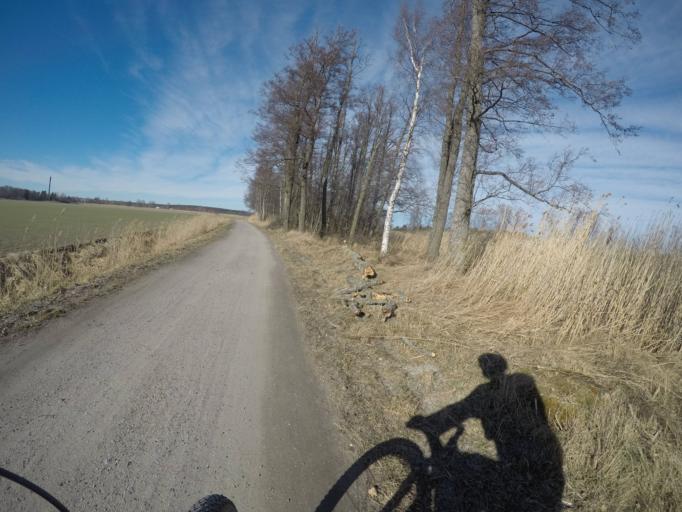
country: SE
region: Soedermanland
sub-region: Eskilstuna Kommun
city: Torshalla
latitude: 59.3953
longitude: 16.4649
